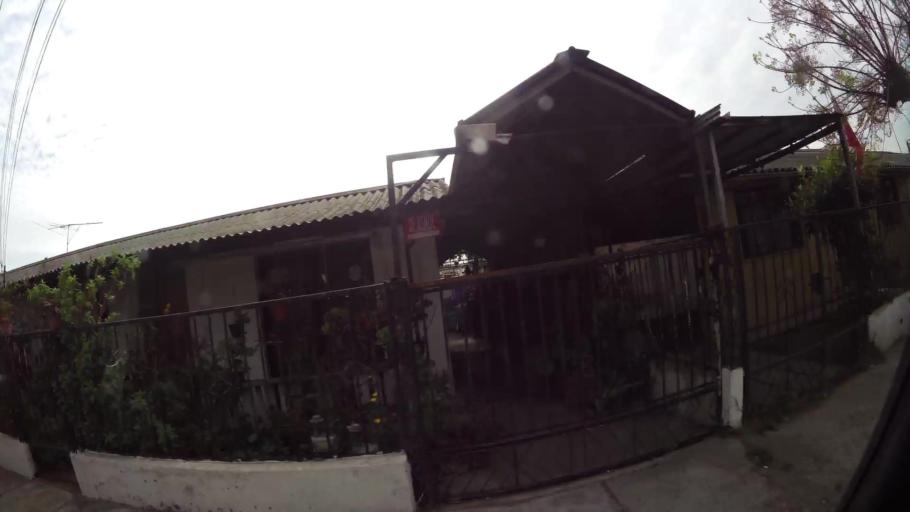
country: CL
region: Santiago Metropolitan
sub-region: Provincia de Santiago
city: Lo Prado
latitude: -33.5147
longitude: -70.7536
